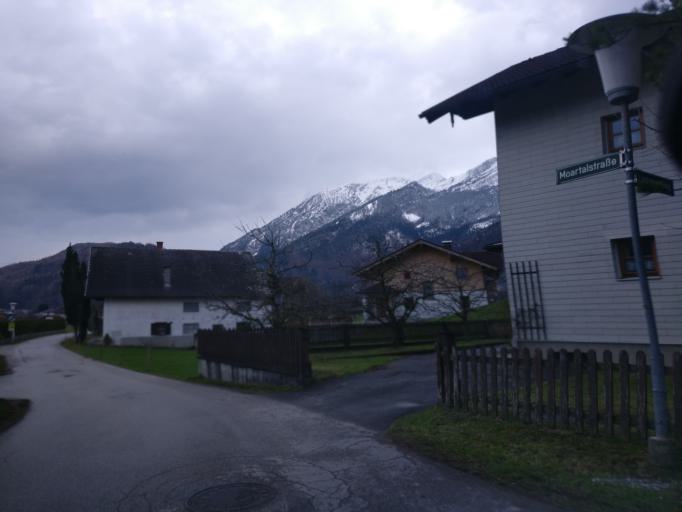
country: AT
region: Salzburg
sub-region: Politischer Bezirk Hallein
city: Golling an der Salzach
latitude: 47.5872
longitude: 13.1676
